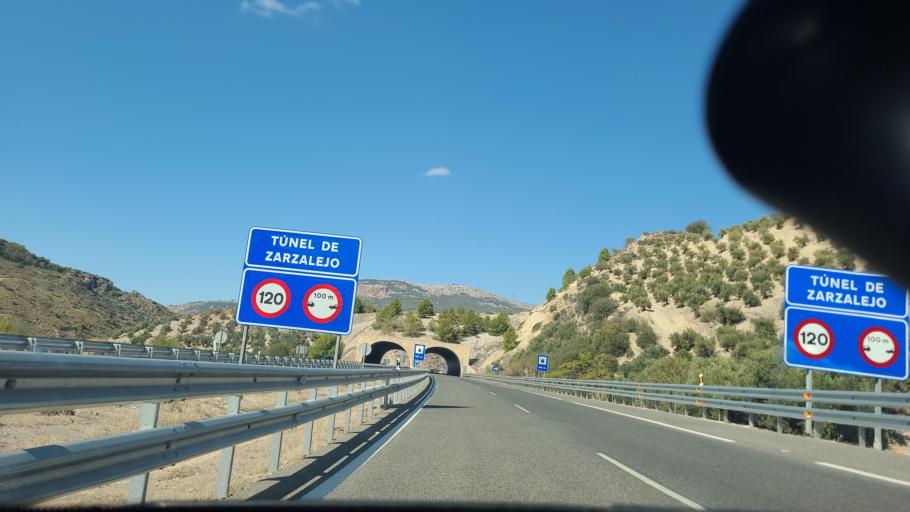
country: ES
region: Andalusia
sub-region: Provincia de Jaen
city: Pegalajar
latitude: 37.7009
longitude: -3.6348
